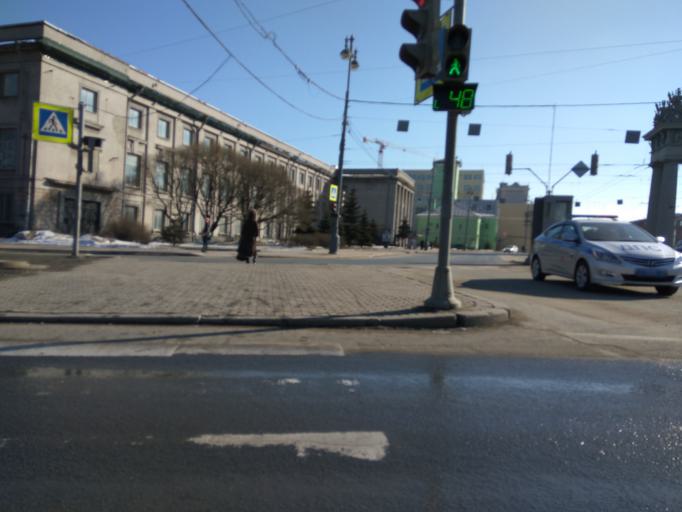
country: RU
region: St.-Petersburg
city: Admiralteisky
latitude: 59.8924
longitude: 30.3201
